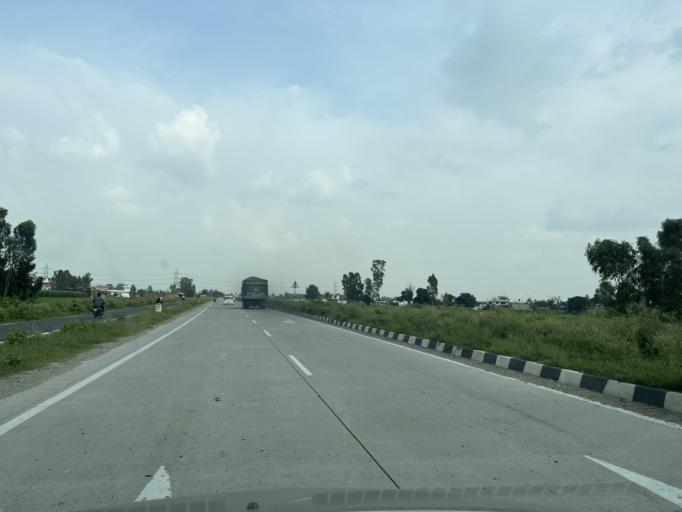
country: IN
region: Uttarakhand
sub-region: Udham Singh Nagar
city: Bazpur
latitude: 29.1504
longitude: 79.0731
